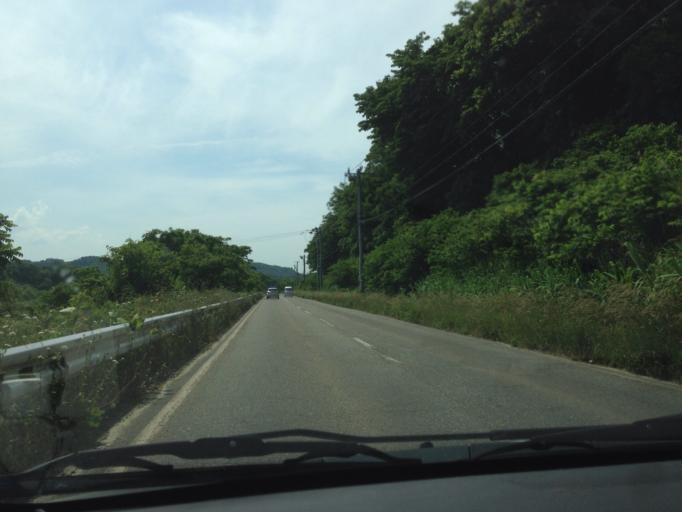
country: JP
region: Fukushima
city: Kitakata
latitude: 37.6107
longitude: 139.8167
